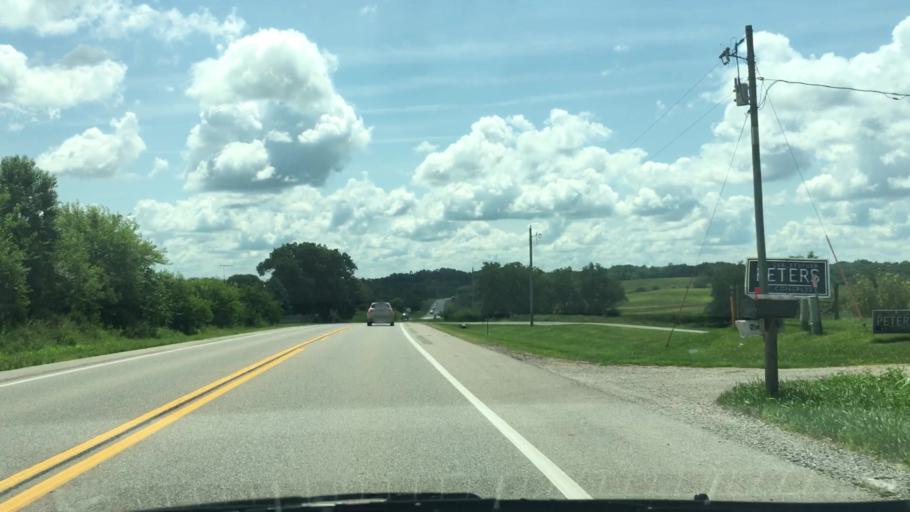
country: US
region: Iowa
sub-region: Johnson County
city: Solon
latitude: 41.7605
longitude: -91.4789
